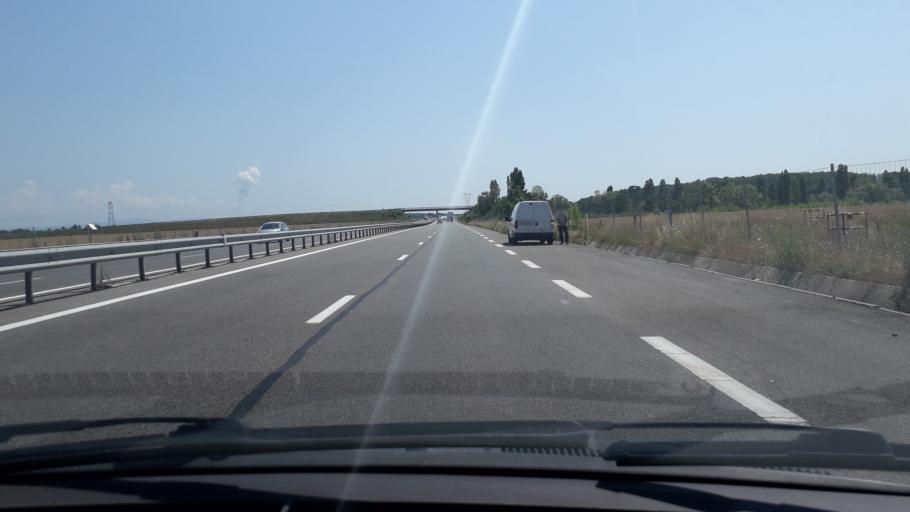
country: FR
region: Rhone-Alpes
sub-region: Departement de l'Isere
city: Janneyrias
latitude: 45.7661
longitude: 5.0935
